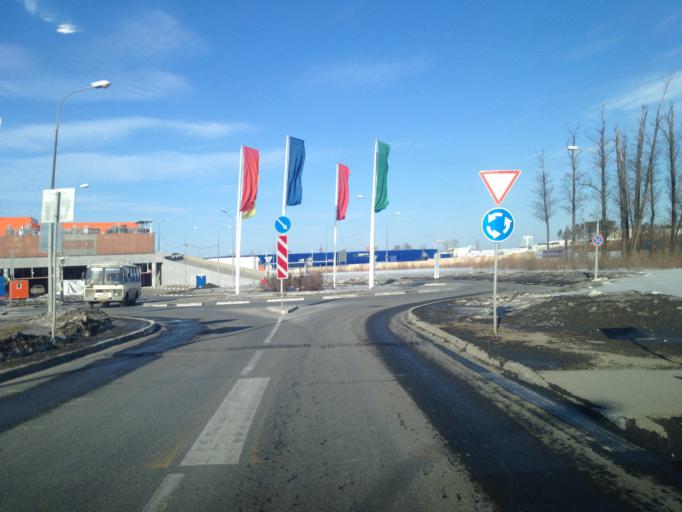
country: RU
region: Sverdlovsk
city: Shirokaya Rechka
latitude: 56.8213
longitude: 60.5085
